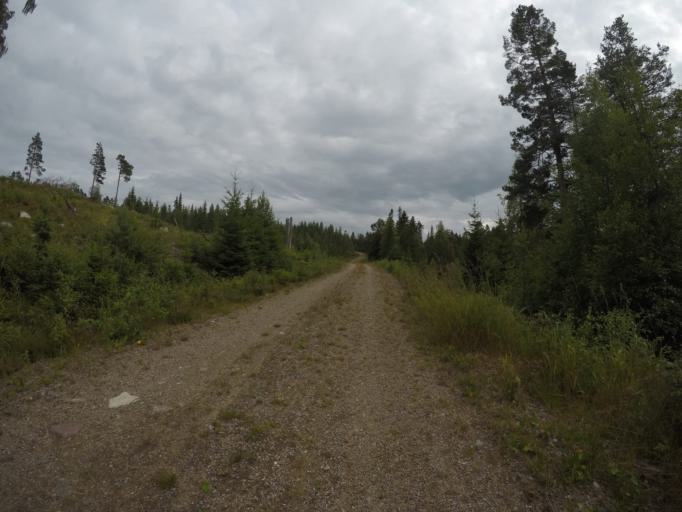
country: SE
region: Vaermland
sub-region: Filipstads Kommun
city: Lesjofors
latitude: 60.2085
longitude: 14.2618
